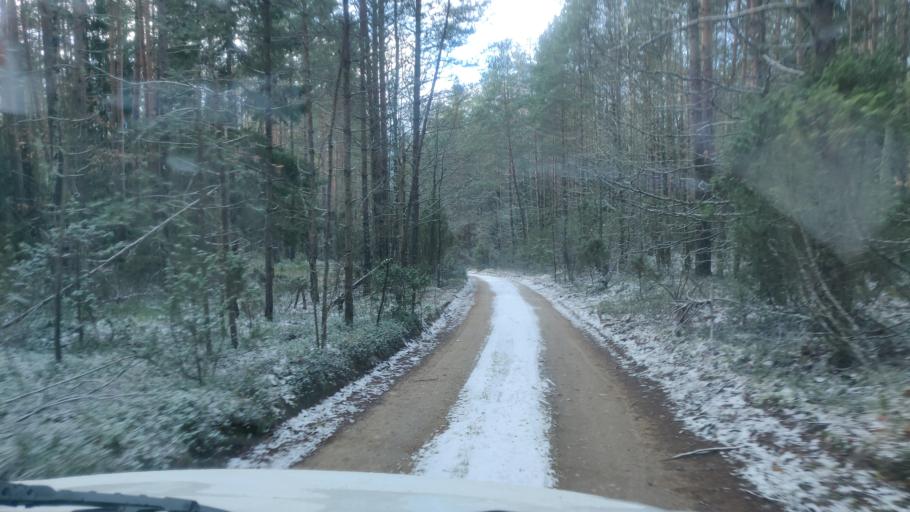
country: LT
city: Trakai
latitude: 54.5665
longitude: 24.9200
